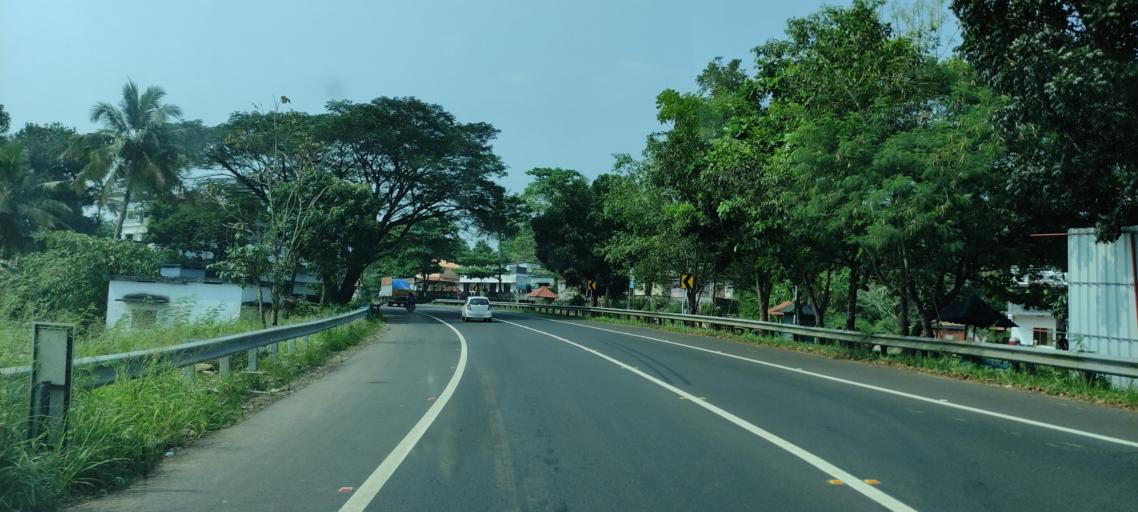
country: IN
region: Kerala
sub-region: Alappuzha
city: Chengannur
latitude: 9.2493
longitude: 76.6675
